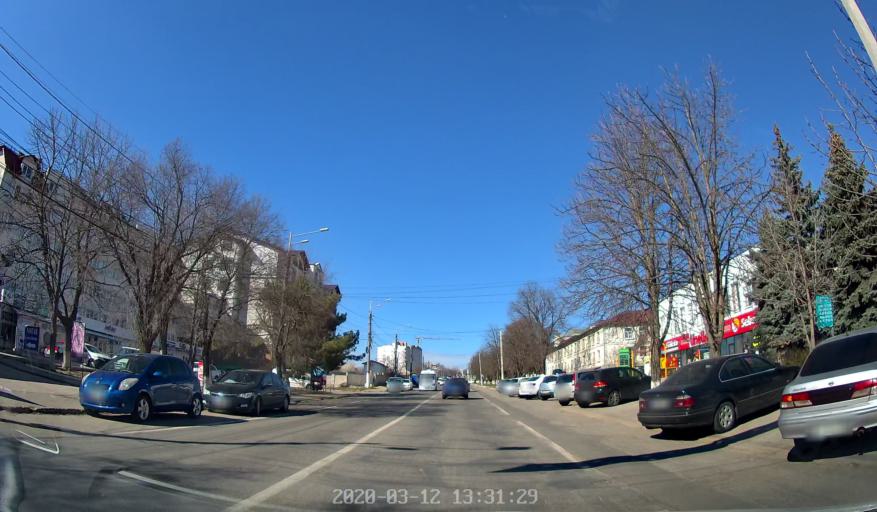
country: MD
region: Laloveni
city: Ialoveni
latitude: 46.9470
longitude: 28.7747
